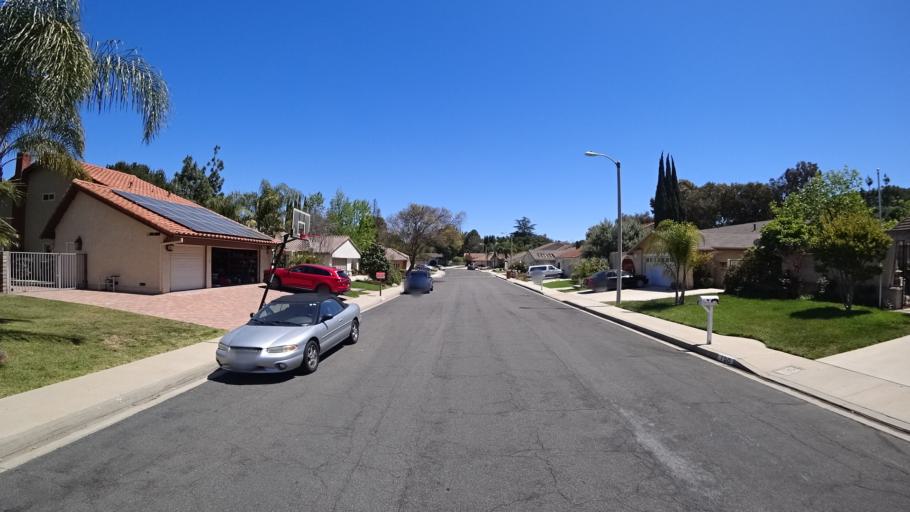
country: US
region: California
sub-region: Ventura County
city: Casa Conejo
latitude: 34.1781
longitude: -118.8969
